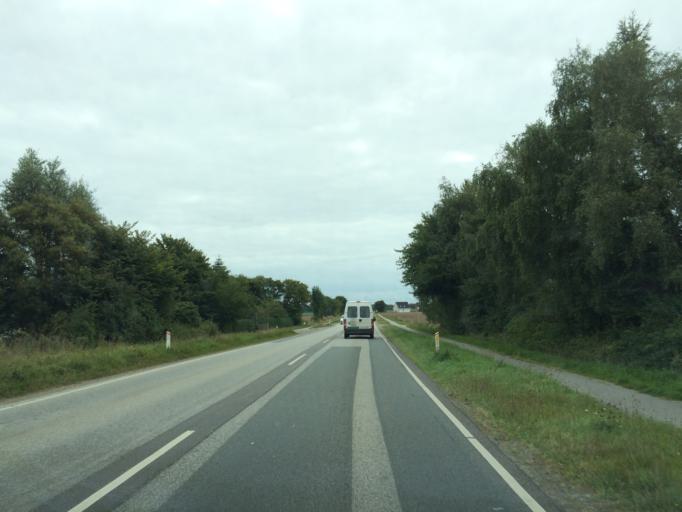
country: DK
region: South Denmark
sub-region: Sonderborg Kommune
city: Broager
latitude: 54.9665
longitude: 9.6712
